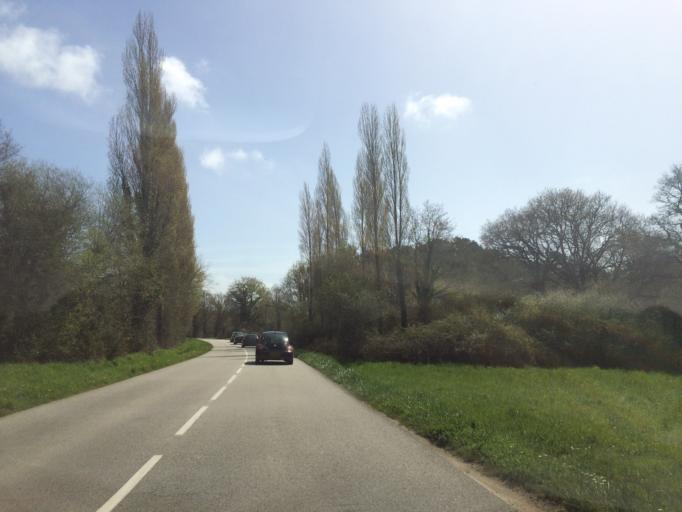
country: FR
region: Brittany
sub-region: Departement du Morbihan
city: Ploemel
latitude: 47.6175
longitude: -3.0553
